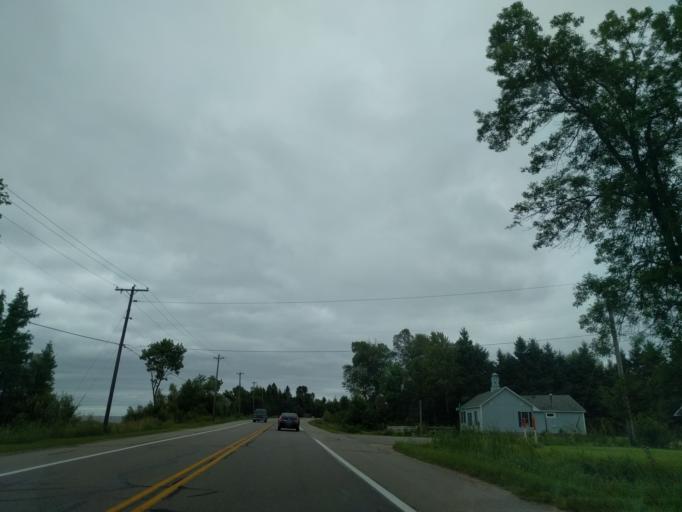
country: US
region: Michigan
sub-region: Delta County
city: Escanaba
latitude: 45.6962
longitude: -87.1011
